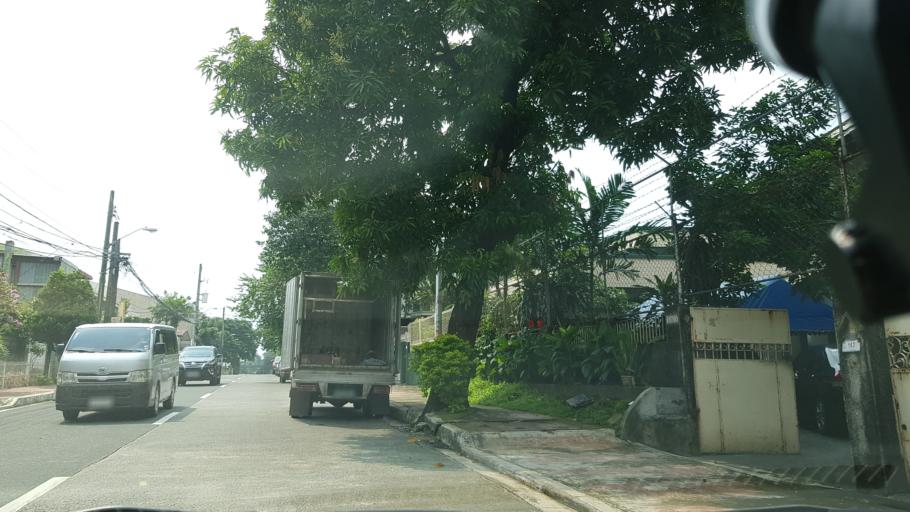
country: PH
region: Metro Manila
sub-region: Quezon City
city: Quezon City
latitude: 14.6304
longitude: 121.0406
